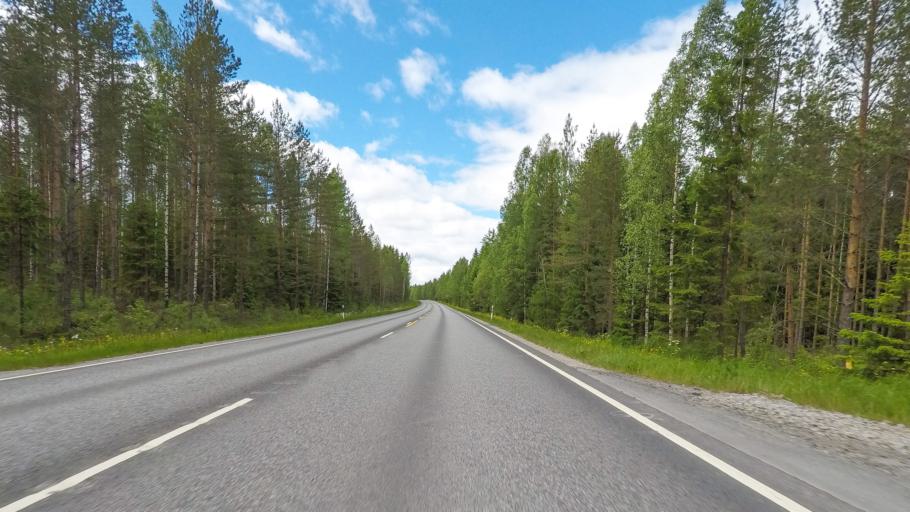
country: FI
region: Central Finland
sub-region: Jyvaeskylae
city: Toivakka
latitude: 62.2116
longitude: 26.2094
